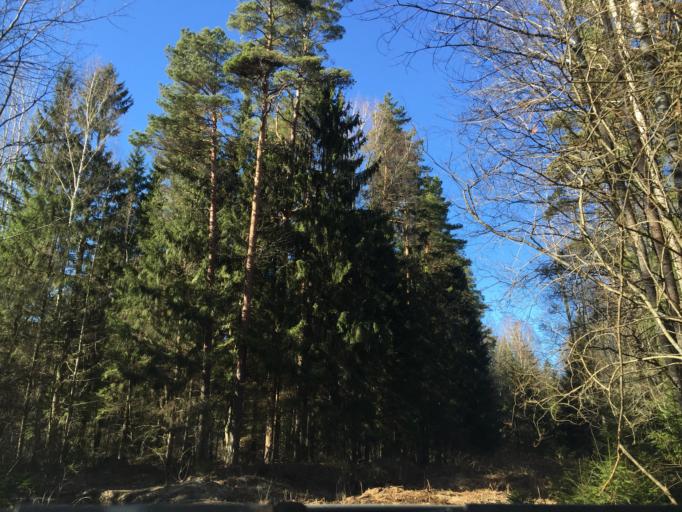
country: LV
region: Incukalns
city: Vangazi
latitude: 57.0948
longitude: 24.5302
